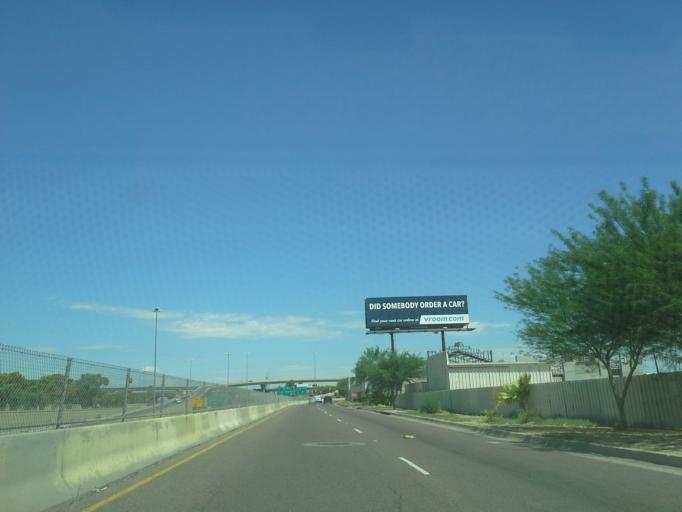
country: US
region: Arizona
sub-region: Maricopa County
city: Phoenix
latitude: 33.4543
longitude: -112.1077
